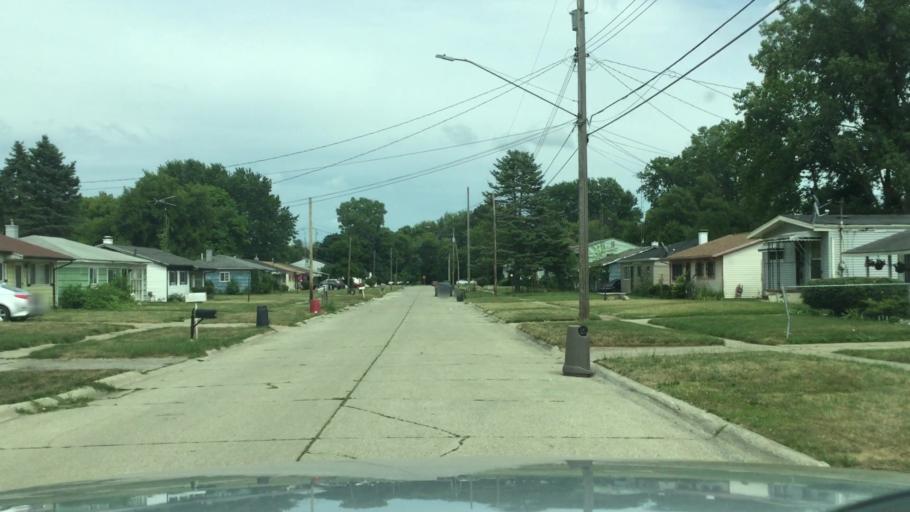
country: US
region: Michigan
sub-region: Genesee County
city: Beecher
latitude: 43.0788
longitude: -83.6811
